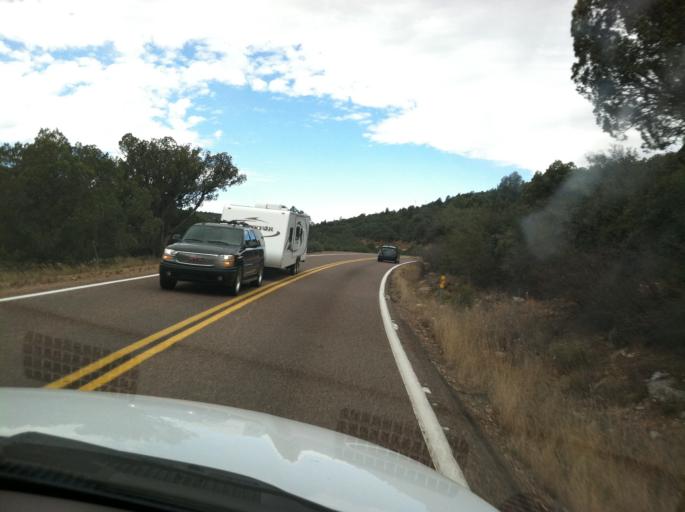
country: US
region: Arizona
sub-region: Gila County
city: Pine
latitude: 34.3162
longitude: -111.3882
